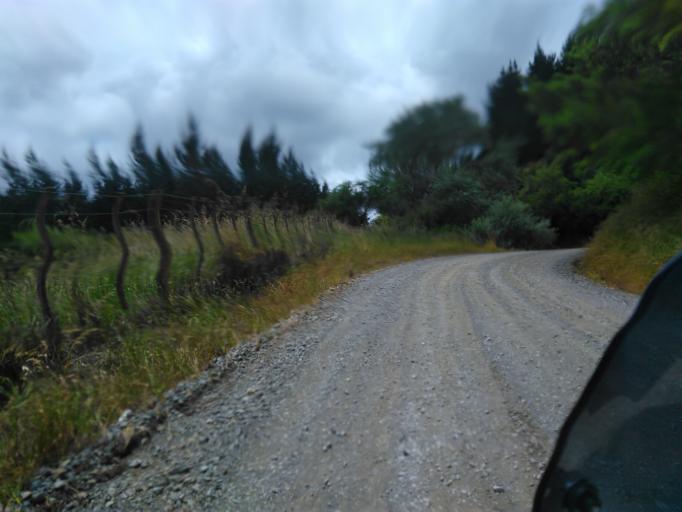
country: NZ
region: Gisborne
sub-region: Gisborne District
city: Gisborne
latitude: -38.0561
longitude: 178.1424
